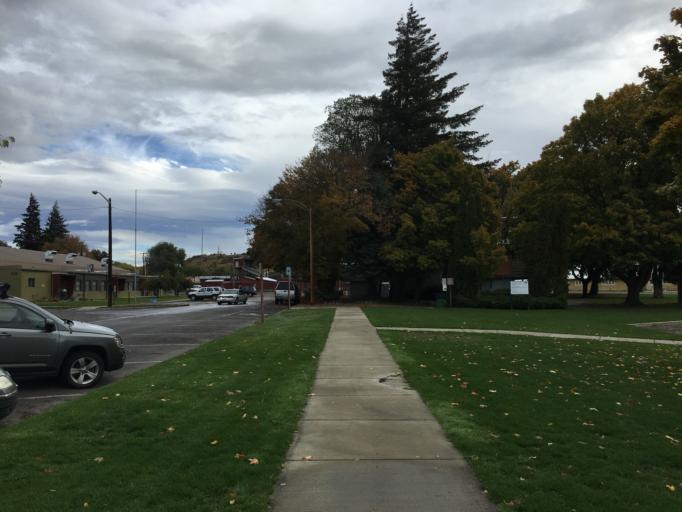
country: US
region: Washington
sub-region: Kittitas County
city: Ellensburg
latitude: 46.9988
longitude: -120.5360
